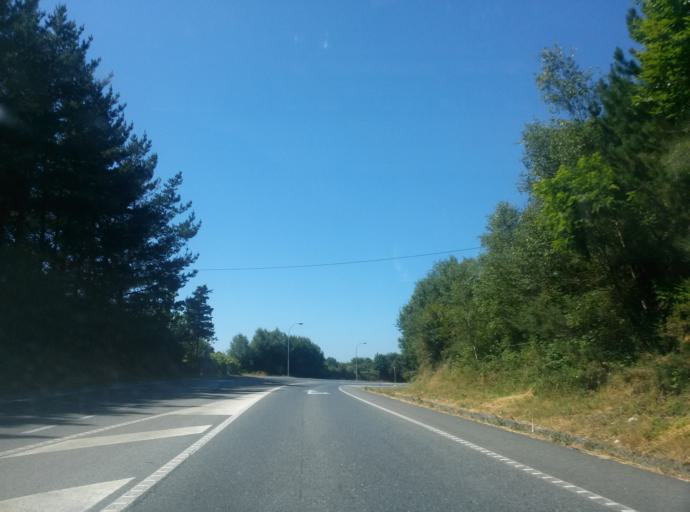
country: ES
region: Galicia
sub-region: Provincia de Lugo
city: Mos
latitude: 43.1263
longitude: -7.4869
